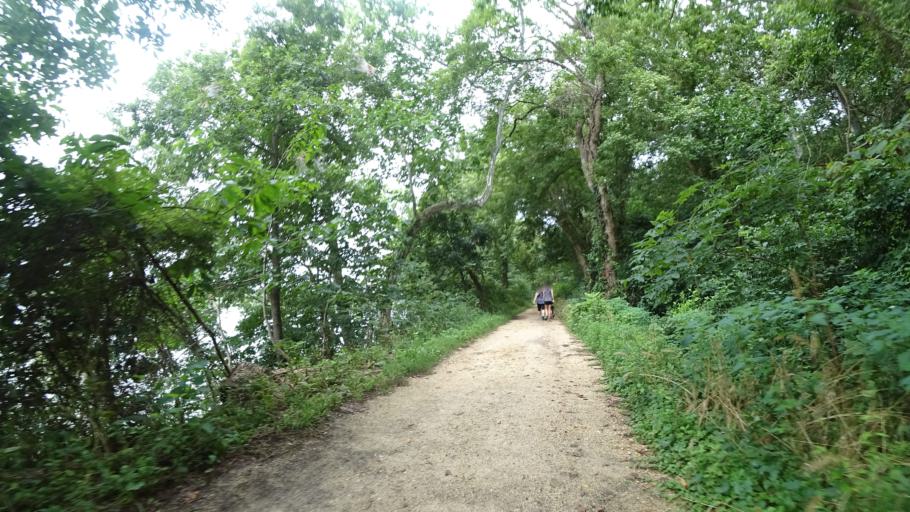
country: US
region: Virginia
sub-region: Loudoun County
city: Lowes Island
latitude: 39.0680
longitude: -77.3558
